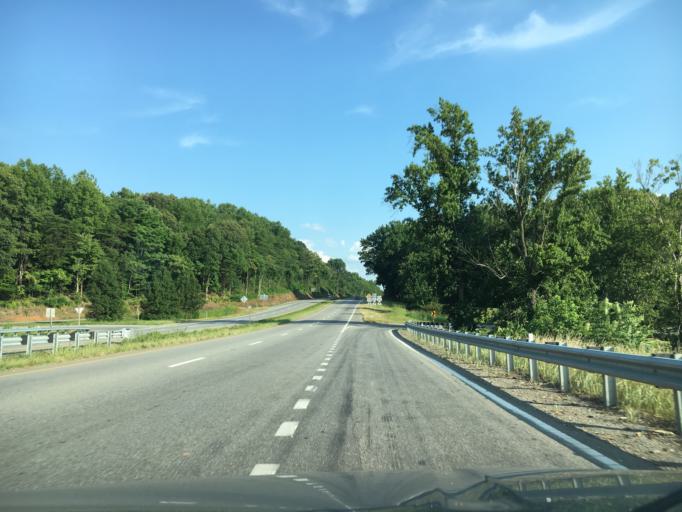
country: US
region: Virginia
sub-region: Franklin County
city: Rocky Mount
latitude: 37.0087
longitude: -79.8727
